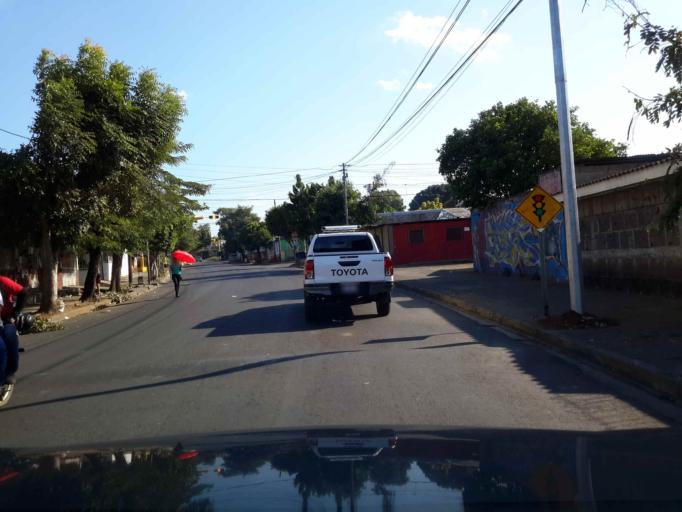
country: NI
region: Managua
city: Managua
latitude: 12.1282
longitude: -86.2515
